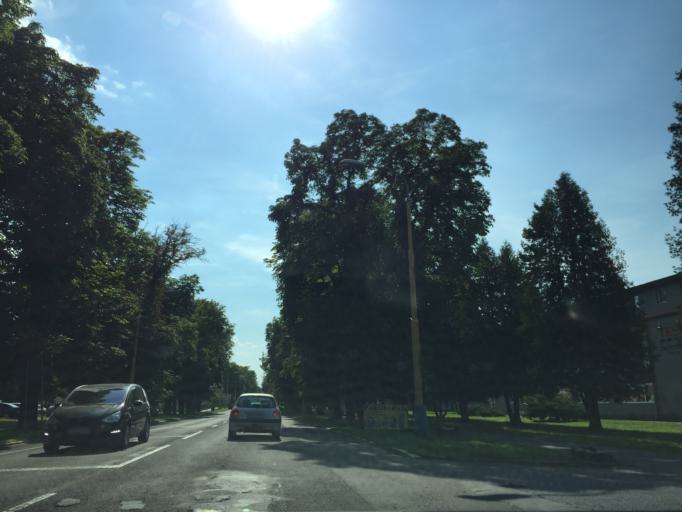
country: SK
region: Kosicky
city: Strazske
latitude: 48.8736
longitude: 21.8396
